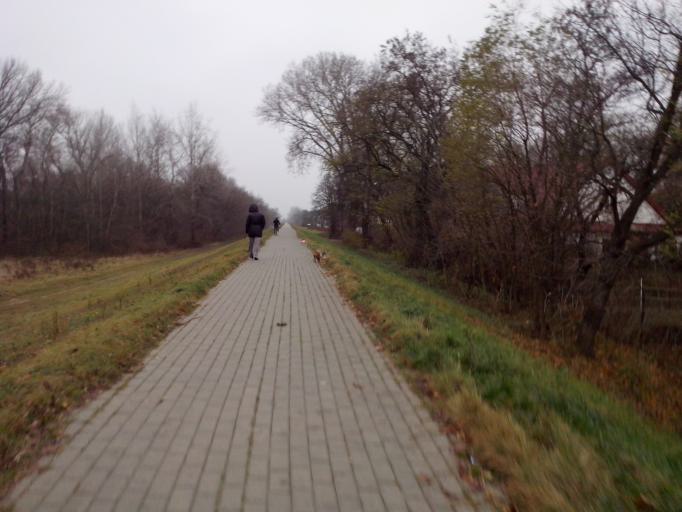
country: PL
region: Masovian Voivodeship
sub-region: Warszawa
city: Bielany
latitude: 52.3289
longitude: 20.9338
